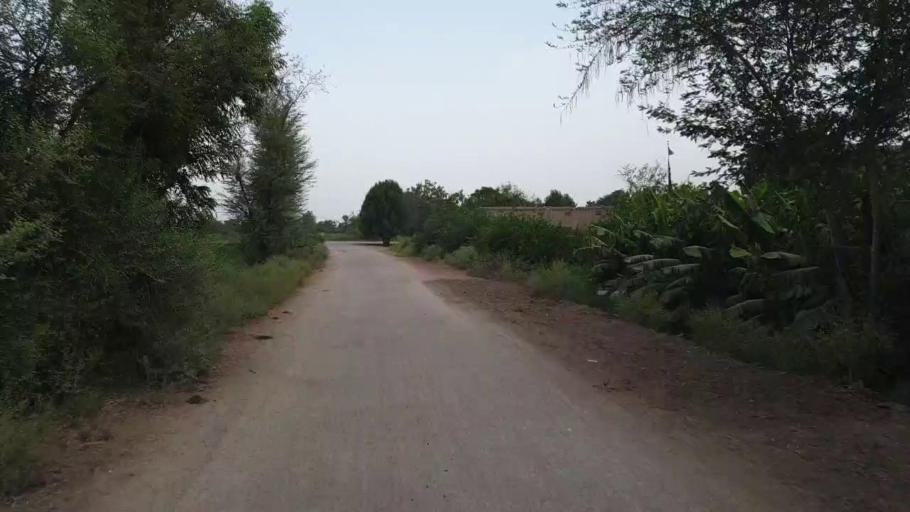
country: PK
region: Sindh
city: Bandhi
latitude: 26.5329
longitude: 68.2042
